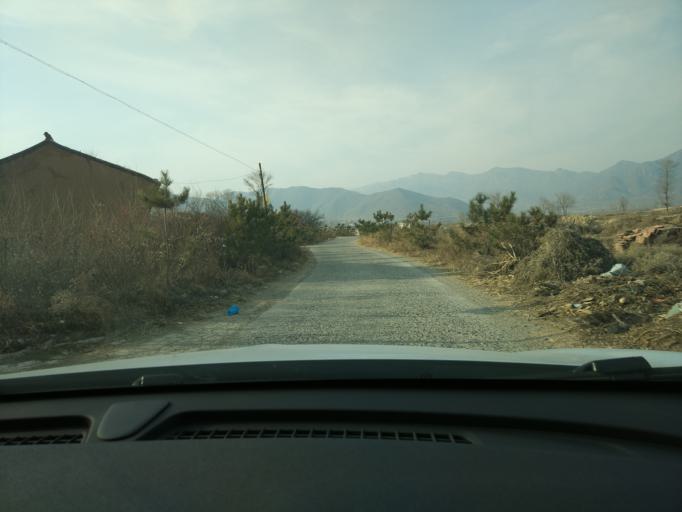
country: CN
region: Hebei
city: Xiwanzi
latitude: 40.8143
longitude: 115.5326
